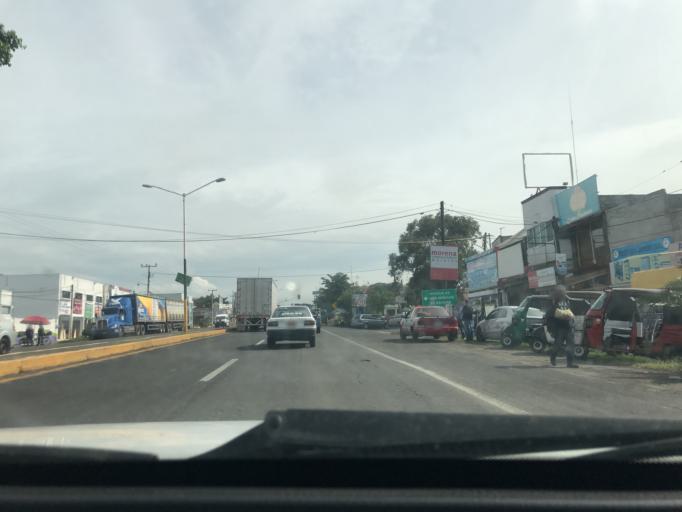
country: MX
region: Morelos
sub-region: Cuautla
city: Tierra Larga (Campo Nuevo)
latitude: 18.8644
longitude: -98.9307
